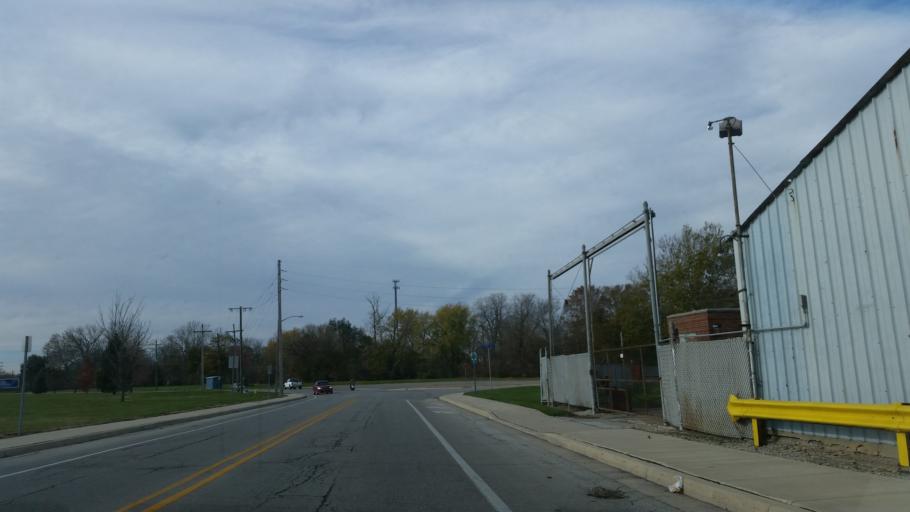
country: US
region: Indiana
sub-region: Howard County
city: Kokomo
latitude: 40.4802
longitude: -86.1452
